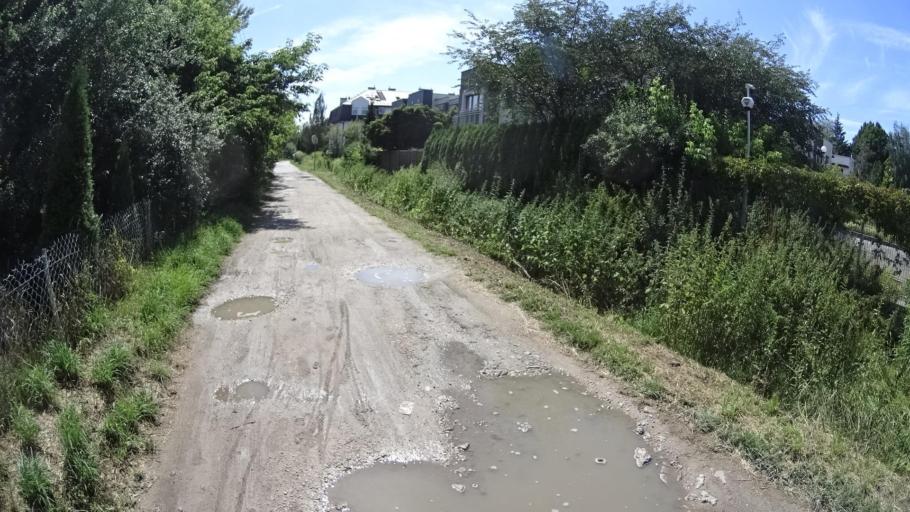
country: PL
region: Masovian Voivodeship
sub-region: Powiat piaseczynski
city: Mysiadlo
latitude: 52.1352
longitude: 21.0125
